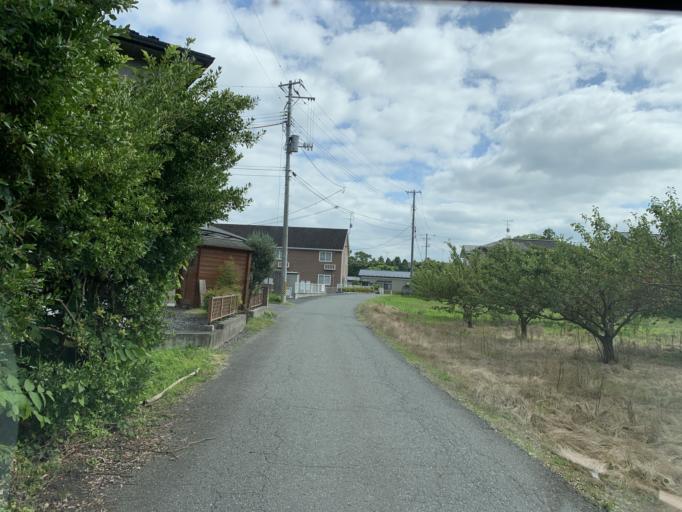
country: JP
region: Iwate
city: Ichinoseki
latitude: 38.9296
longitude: 141.0968
